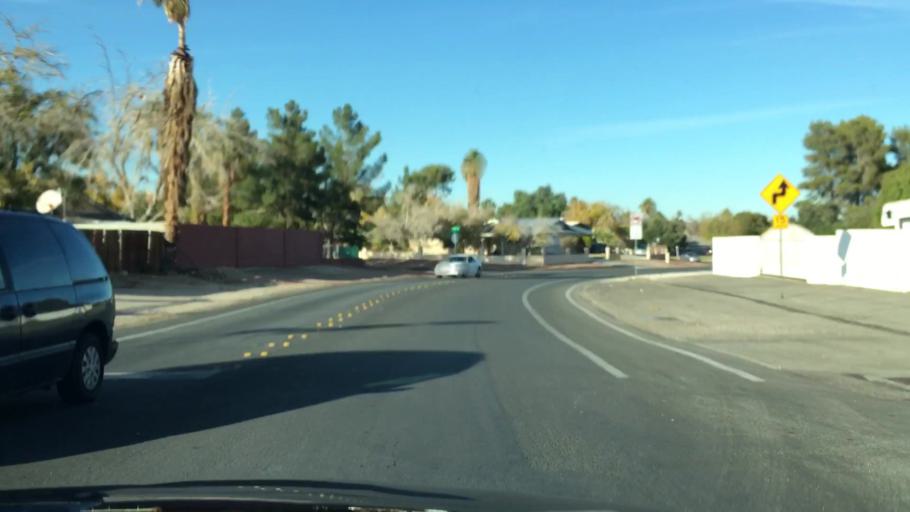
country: US
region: Nevada
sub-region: Clark County
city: Paradise
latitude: 36.1048
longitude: -115.1280
